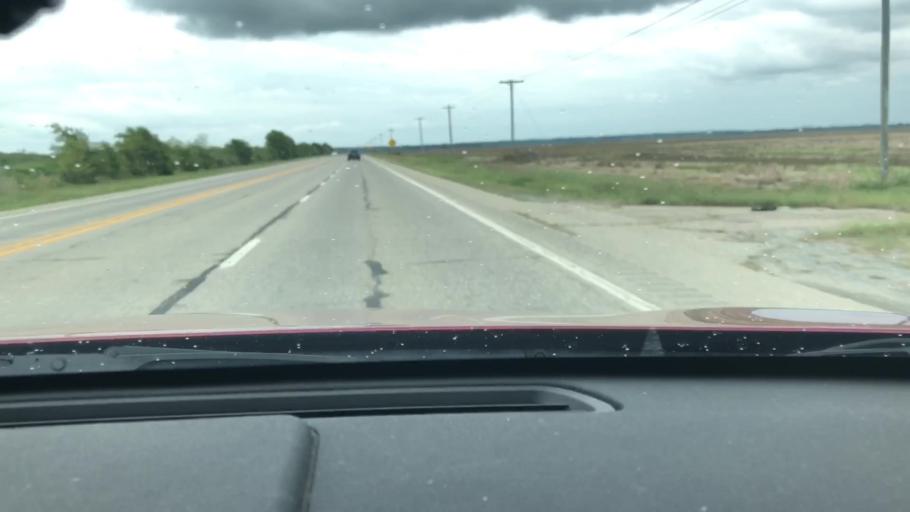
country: US
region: Arkansas
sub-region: Lafayette County
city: Lewisville
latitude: 33.4122
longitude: -93.7843
